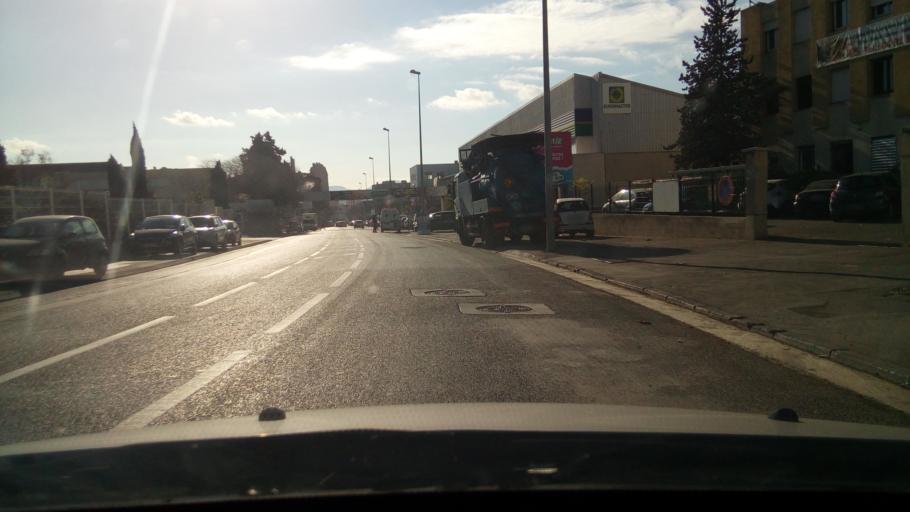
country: FR
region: Provence-Alpes-Cote d'Azur
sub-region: Departement des Bouches-du-Rhone
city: Marseille 14
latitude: 43.3339
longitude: 5.3747
